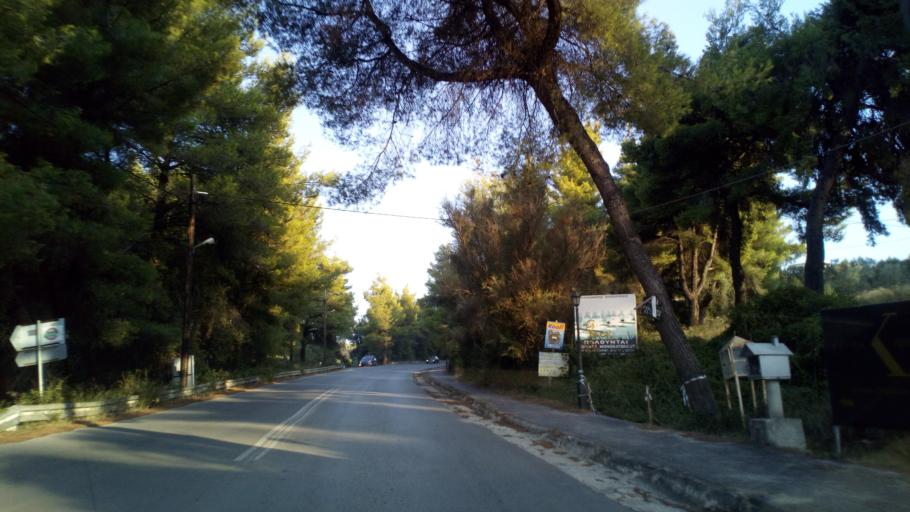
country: GR
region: Central Macedonia
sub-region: Nomos Chalkidikis
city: Pefkochori
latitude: 39.9496
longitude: 23.6725
